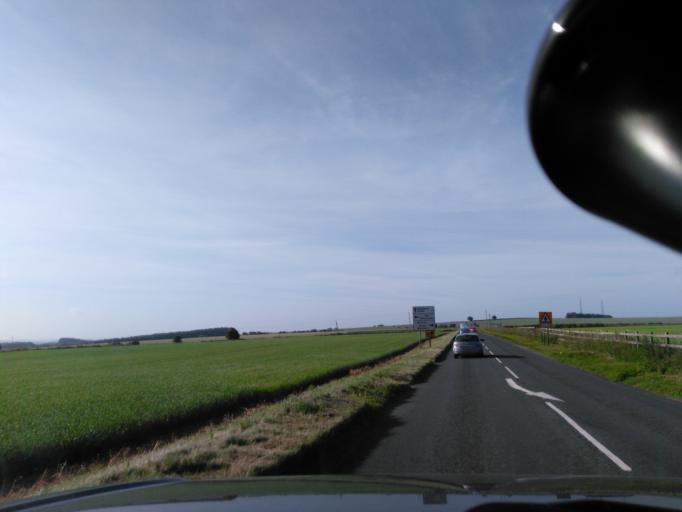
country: GB
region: England
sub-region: Wiltshire
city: Woodford
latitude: 51.1301
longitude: -1.8565
